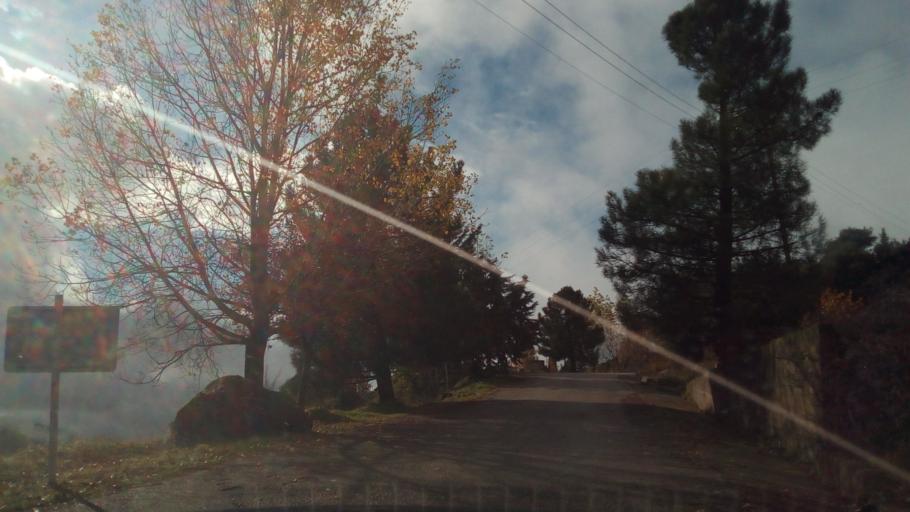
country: GR
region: West Greece
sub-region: Nomos Aitolias kai Akarnanias
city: Nafpaktos
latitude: 38.5396
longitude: 21.9290
